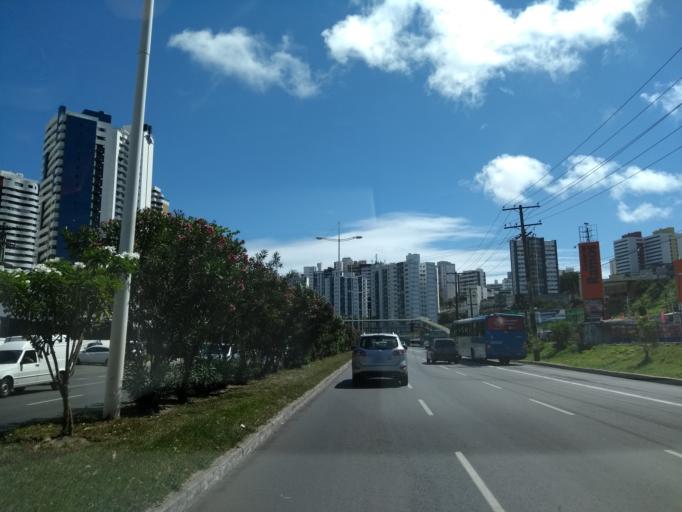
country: BR
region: Bahia
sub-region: Salvador
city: Salvador
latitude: -12.9906
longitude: -38.4738
